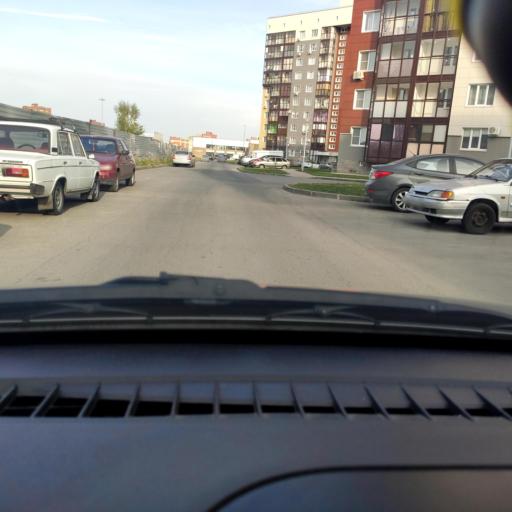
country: RU
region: Samara
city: Tol'yatti
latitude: 53.5297
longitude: 49.3416
